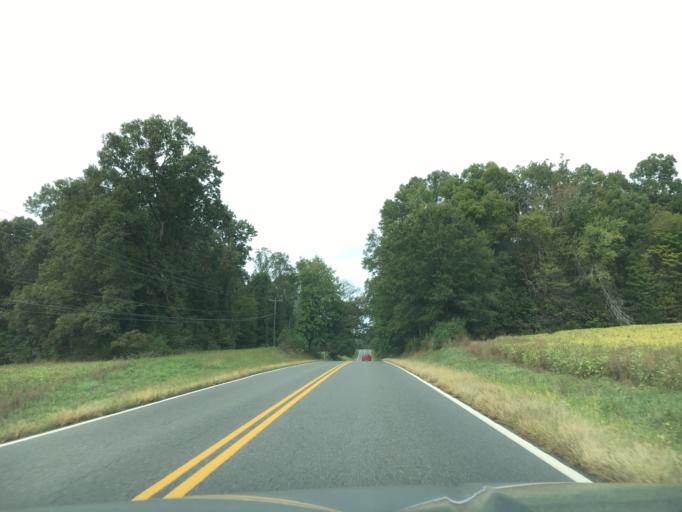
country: US
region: Virginia
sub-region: Goochland County
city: Goochland
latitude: 37.7364
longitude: -77.8415
